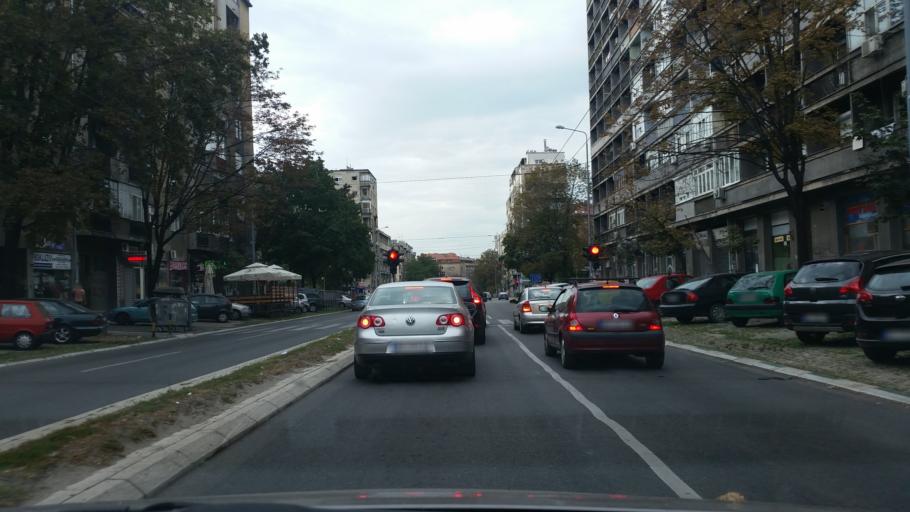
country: RS
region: Central Serbia
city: Belgrade
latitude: 44.8102
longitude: 20.4803
